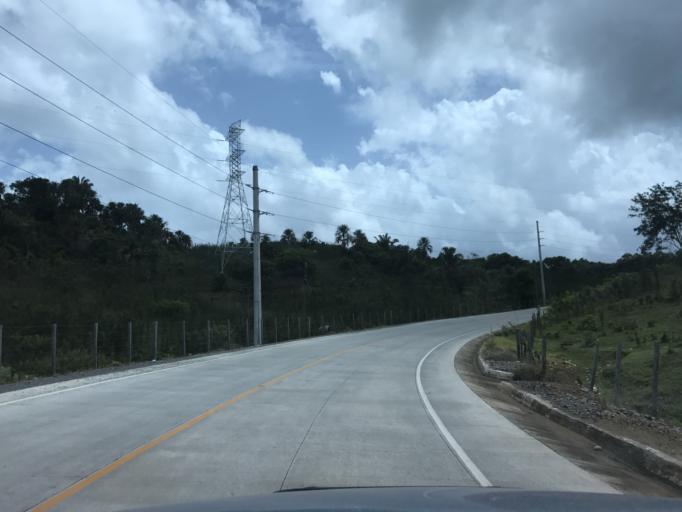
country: GT
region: Izabal
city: Morales
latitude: 15.6224
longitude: -89.0657
